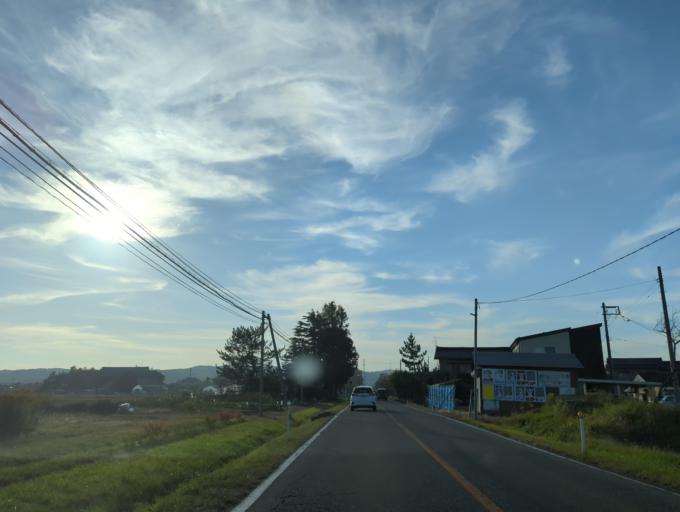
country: JP
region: Niigata
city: Mitsuke
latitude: 37.5551
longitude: 138.8380
